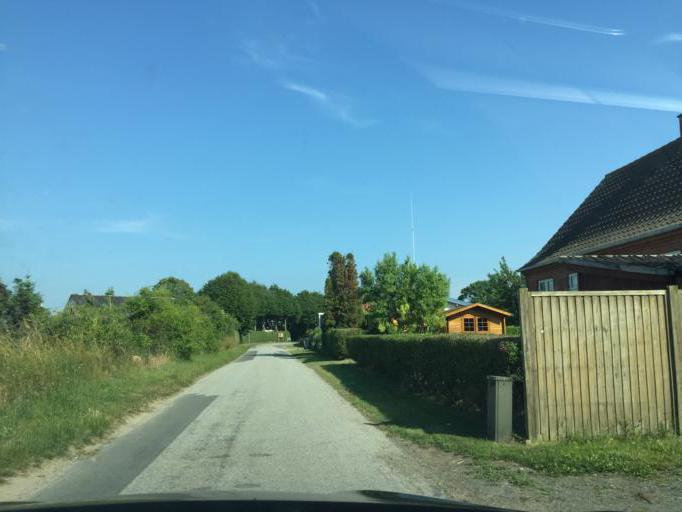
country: DK
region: Zealand
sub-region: Slagelse Kommune
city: Skaelskor
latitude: 55.2150
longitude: 11.1872
